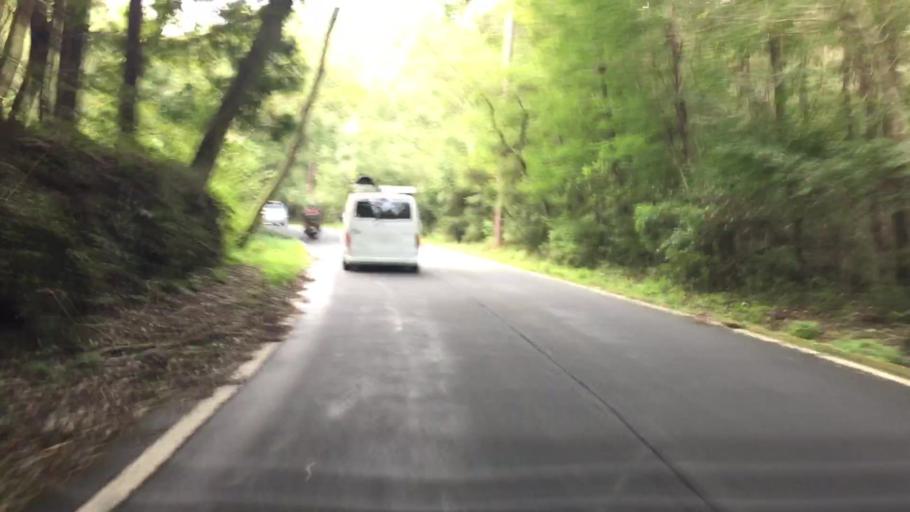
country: JP
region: Shizuoka
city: Fujinomiya
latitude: 35.3651
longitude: 138.5889
